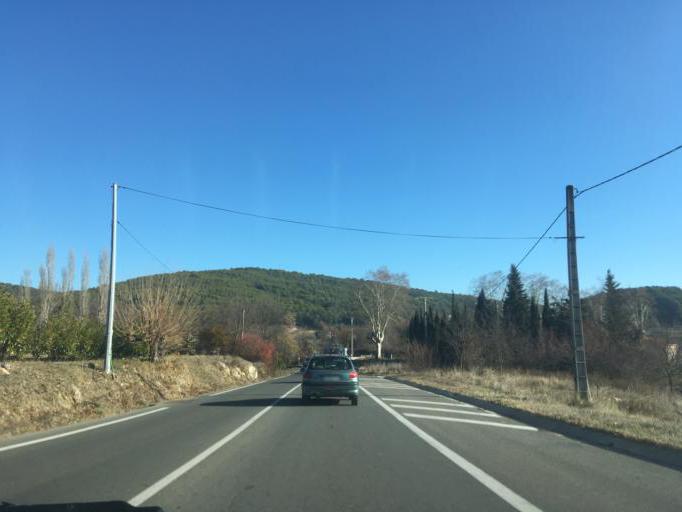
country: FR
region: Provence-Alpes-Cote d'Azur
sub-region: Departement du Var
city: Flayosc
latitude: 43.5340
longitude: 6.4070
